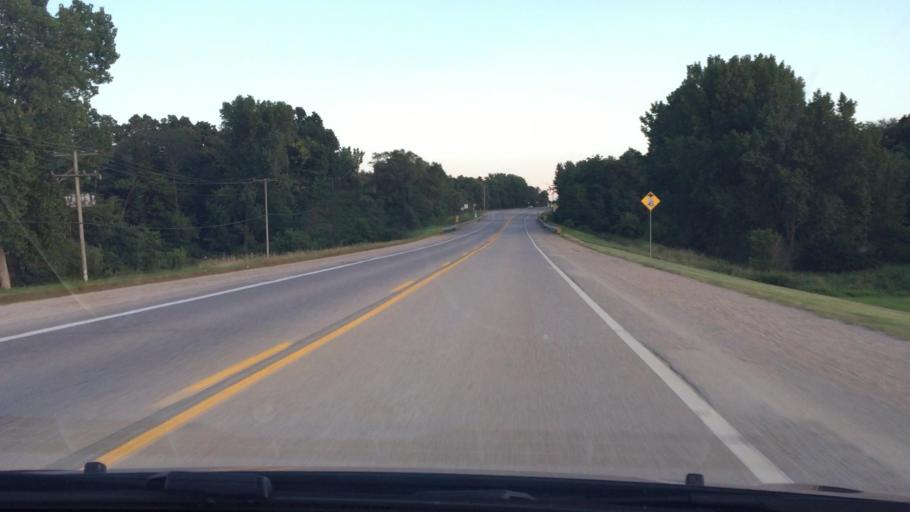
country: US
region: Iowa
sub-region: Muscatine County
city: Muscatine
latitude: 41.4614
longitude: -91.0322
